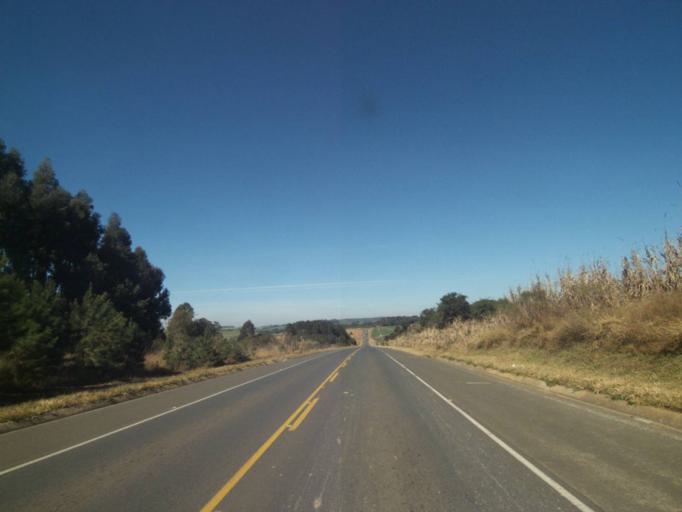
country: BR
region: Parana
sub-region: Tibagi
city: Tibagi
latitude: -24.5301
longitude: -50.4479
